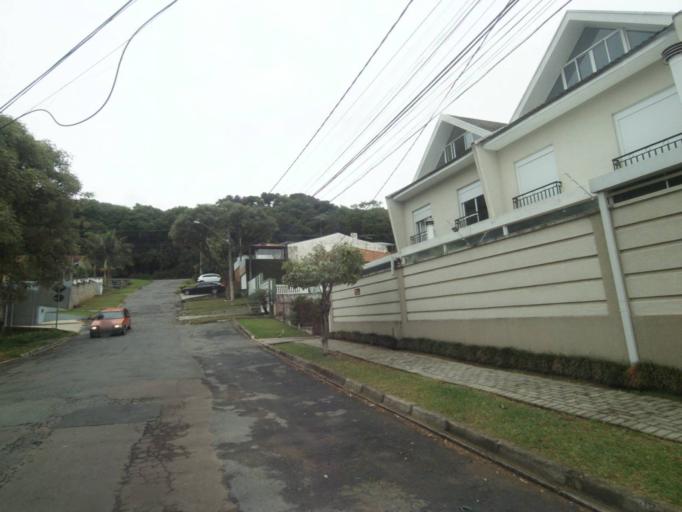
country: BR
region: Parana
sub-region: Curitiba
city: Curitiba
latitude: -25.4279
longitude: -49.3284
